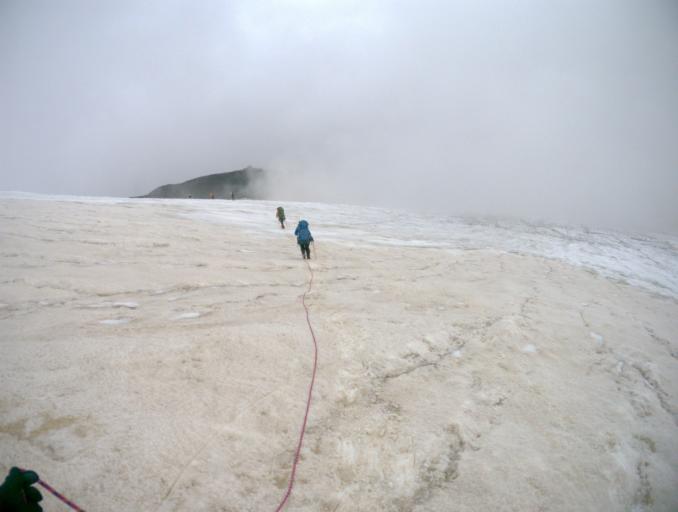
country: RU
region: Kabardino-Balkariya
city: Terskol
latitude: 43.3675
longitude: 42.4949
